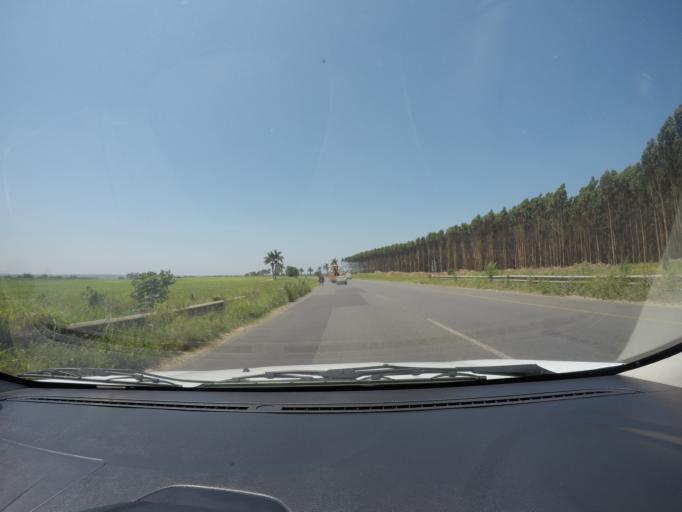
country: ZA
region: KwaZulu-Natal
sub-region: uThungulu District Municipality
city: eSikhawini
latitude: -28.8169
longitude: 31.9533
